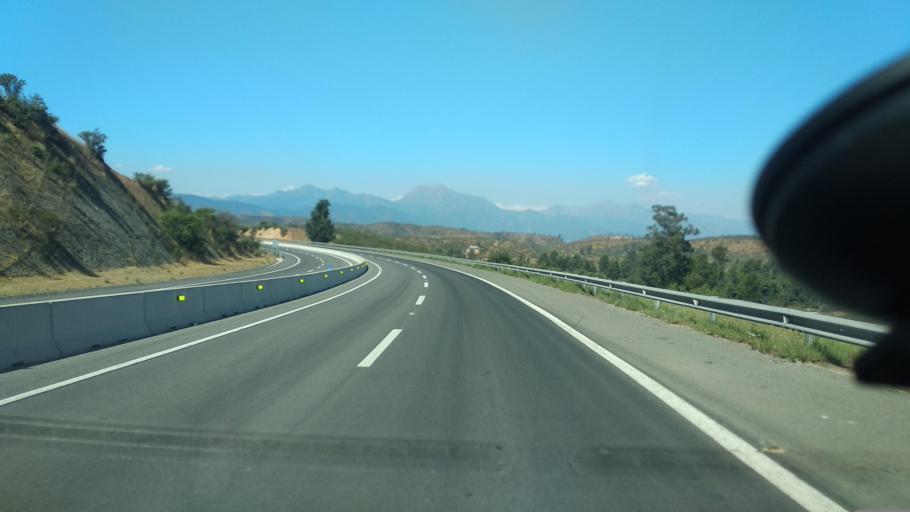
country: CL
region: Valparaiso
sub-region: Provincia de Marga Marga
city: Villa Alemana
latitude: -33.0443
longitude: -71.3216
